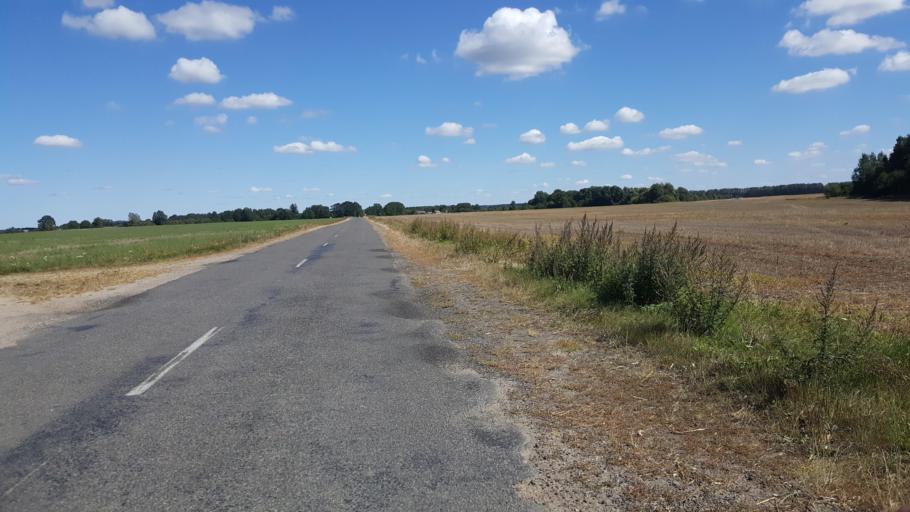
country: BY
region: Brest
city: Vysokaye
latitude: 52.2767
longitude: 23.3293
